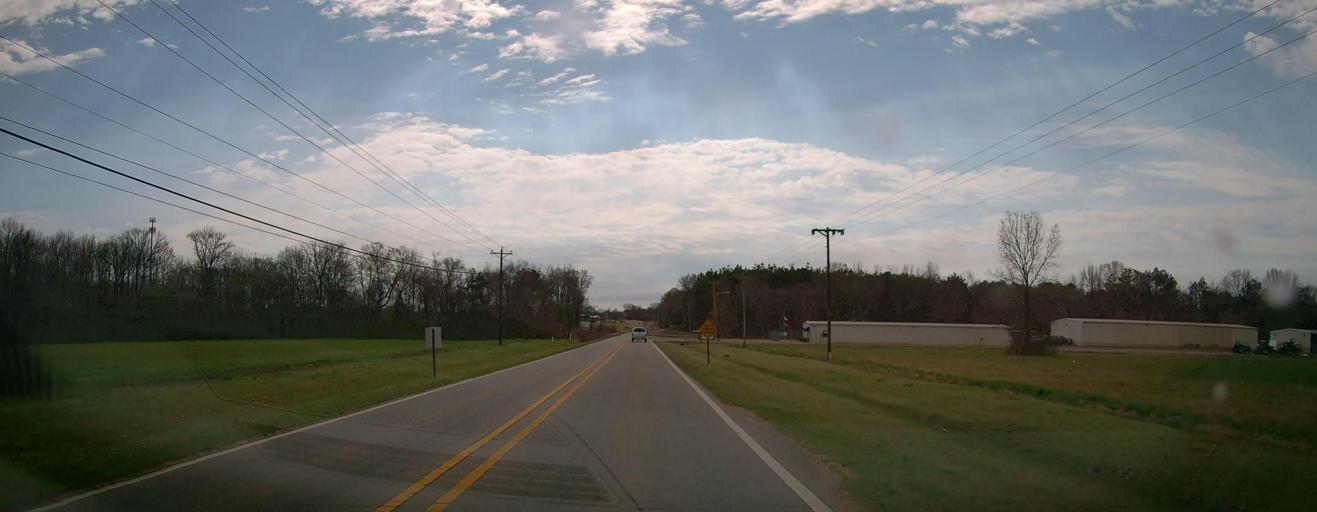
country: US
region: Mississippi
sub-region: De Soto County
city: Olive Branch
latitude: 34.9471
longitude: -89.8098
